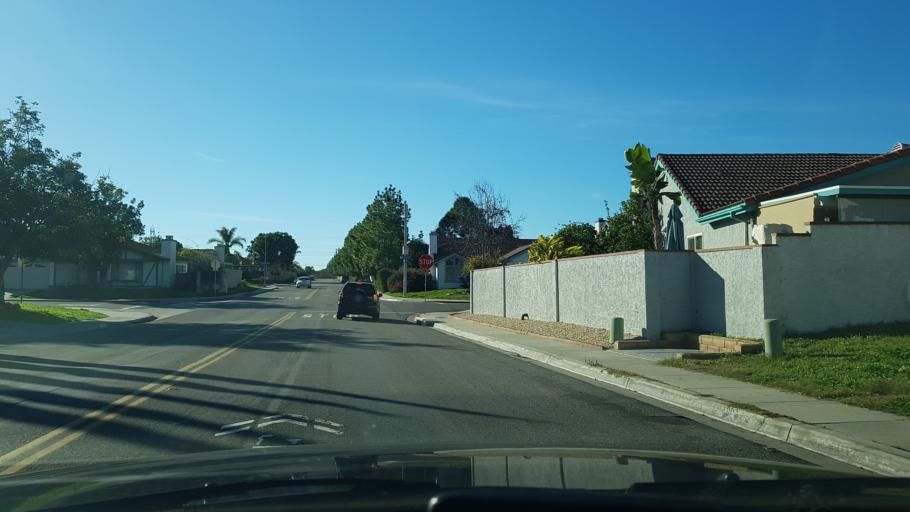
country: US
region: California
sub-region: San Diego County
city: Fairbanks Ranch
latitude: 32.9055
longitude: -117.1642
